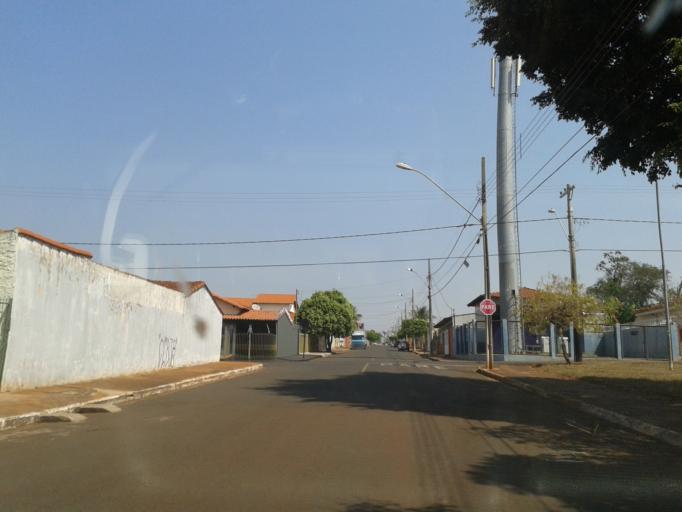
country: BR
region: Minas Gerais
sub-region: Ituiutaba
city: Ituiutaba
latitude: -18.9752
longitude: -49.4726
